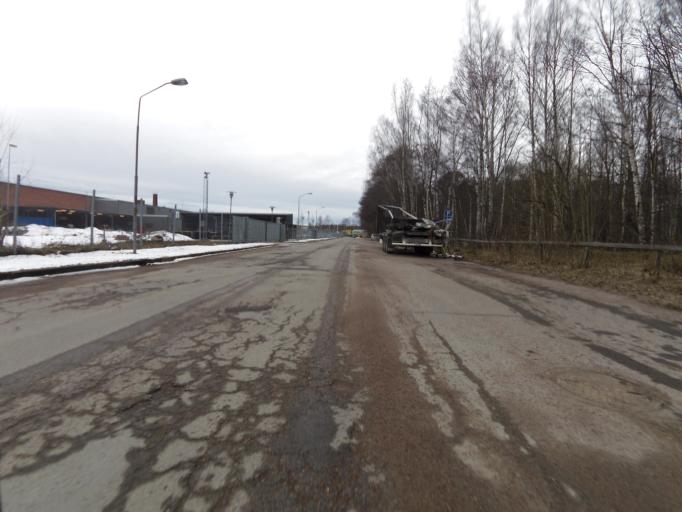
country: SE
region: Gaevleborg
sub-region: Gavle Kommun
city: Gavle
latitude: 60.6882
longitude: 17.1596
